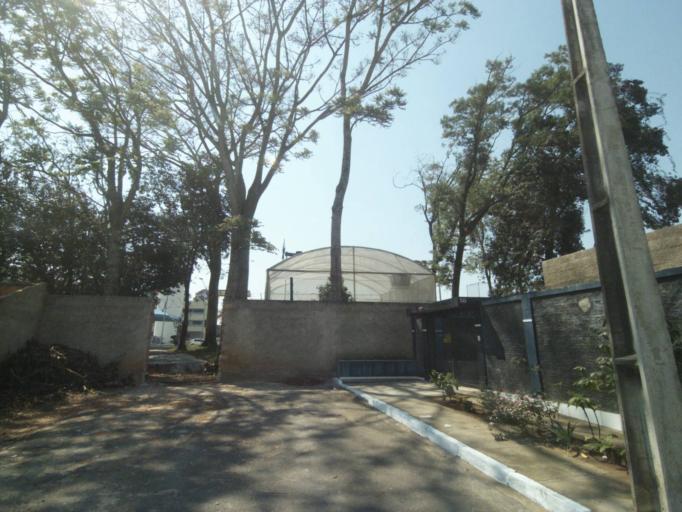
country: BR
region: Parana
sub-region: Curitiba
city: Curitiba
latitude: -25.4825
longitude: -49.2999
